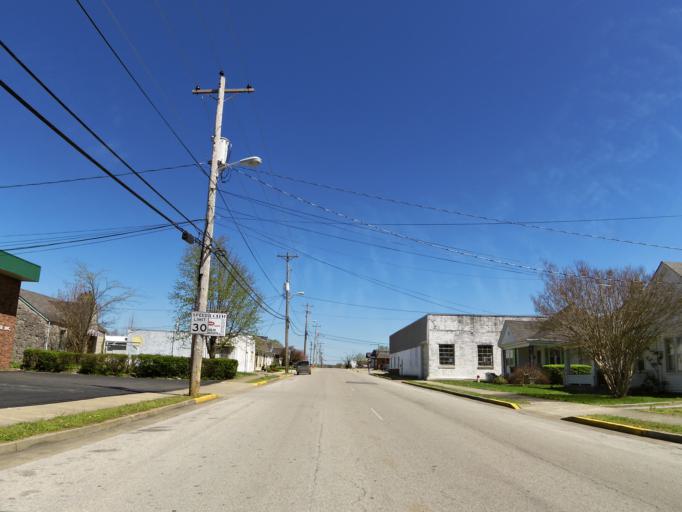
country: US
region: Kentucky
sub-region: Warren County
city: Bowling Green
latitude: 36.9974
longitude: -86.4336
